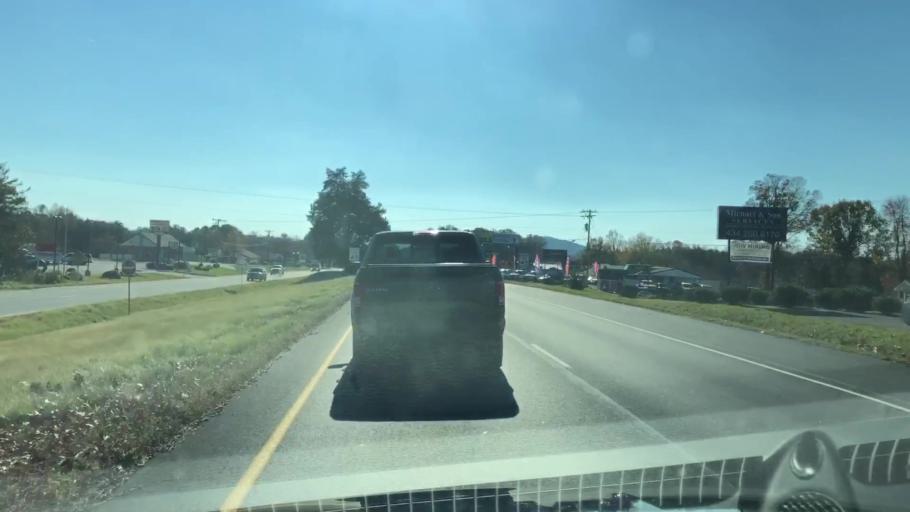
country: US
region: Virginia
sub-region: Greene County
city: Ruckersville
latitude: 38.2279
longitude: -78.3730
